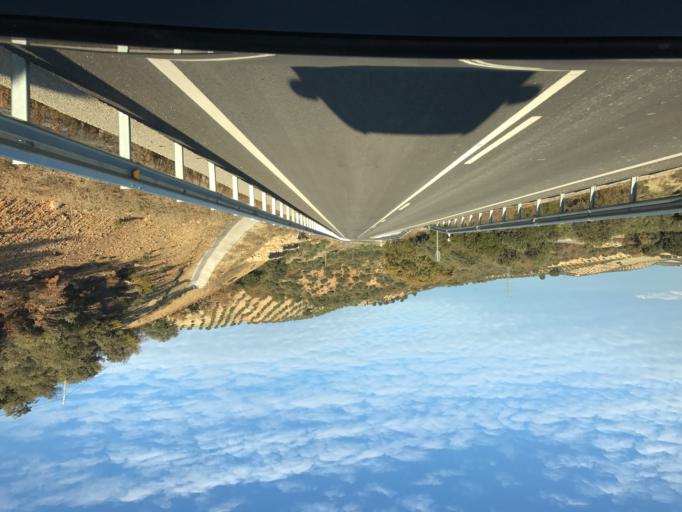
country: ES
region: Andalusia
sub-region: Provincia de Granada
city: Pinar
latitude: 37.4316
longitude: -3.4782
